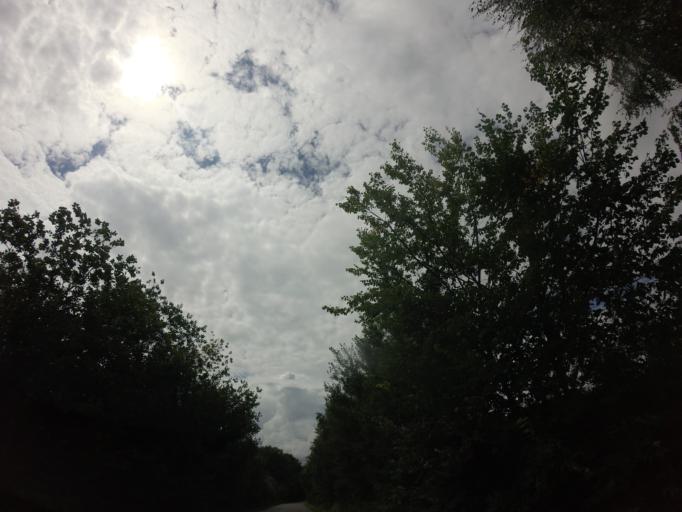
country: PL
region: Lublin Voivodeship
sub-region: Powiat opolski
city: Wilkow
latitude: 51.2739
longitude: 21.9272
